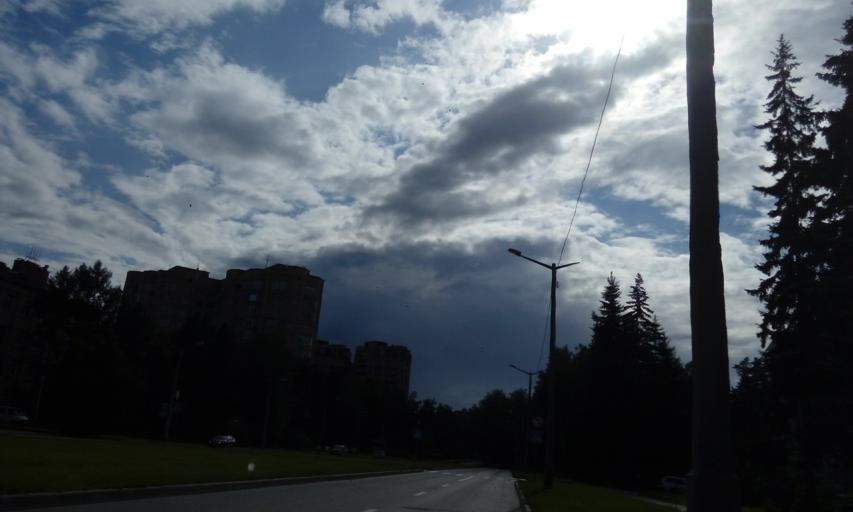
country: RU
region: Novosibirsk
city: Akademgorodok
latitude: 54.8464
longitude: 83.1051
